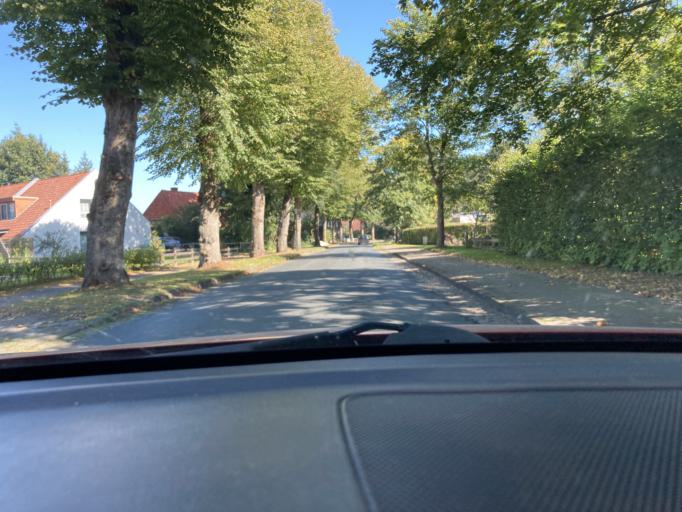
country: DE
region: Lower Saxony
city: Reessum
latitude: 53.1579
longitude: 9.2084
